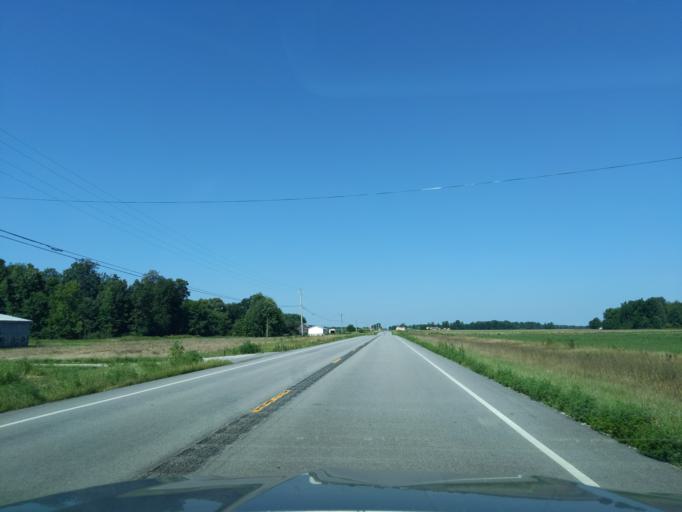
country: US
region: Indiana
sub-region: Ripley County
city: Versailles
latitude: 39.0750
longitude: -85.2813
